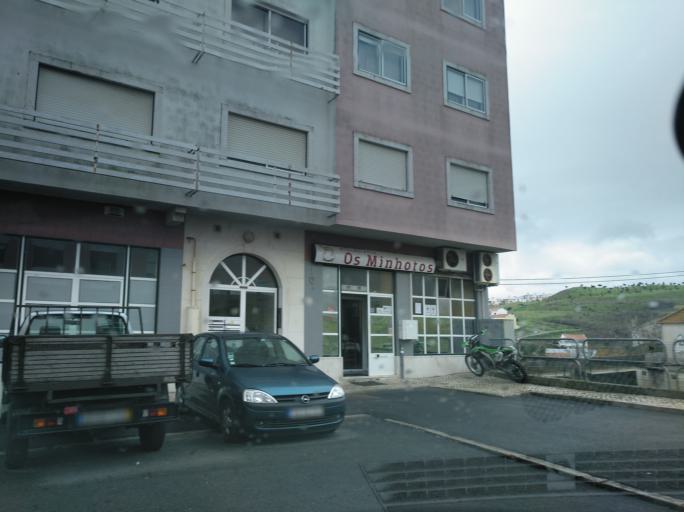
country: PT
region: Lisbon
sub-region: Odivelas
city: Famoes
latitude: 38.7950
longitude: -9.2213
